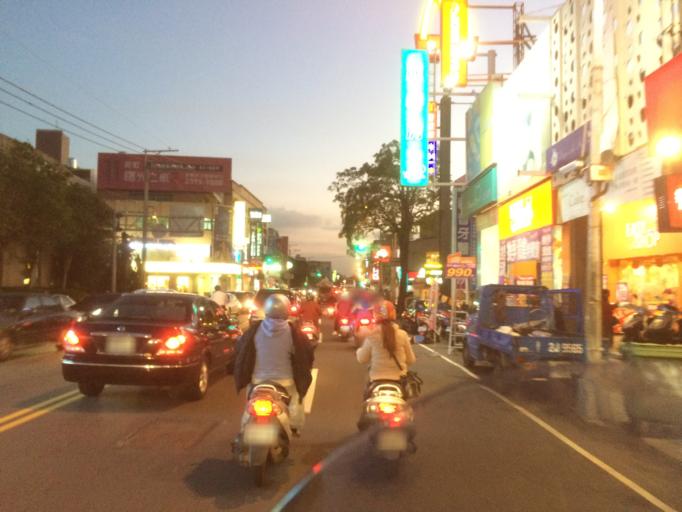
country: TW
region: Taiwan
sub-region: Taichung City
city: Taichung
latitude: 24.1755
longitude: 120.7191
